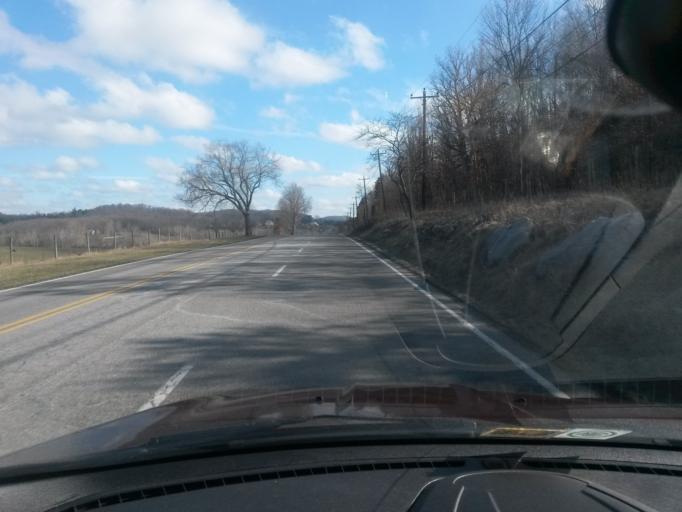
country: US
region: Virginia
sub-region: Augusta County
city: Jolivue
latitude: 38.0891
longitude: -79.0918
